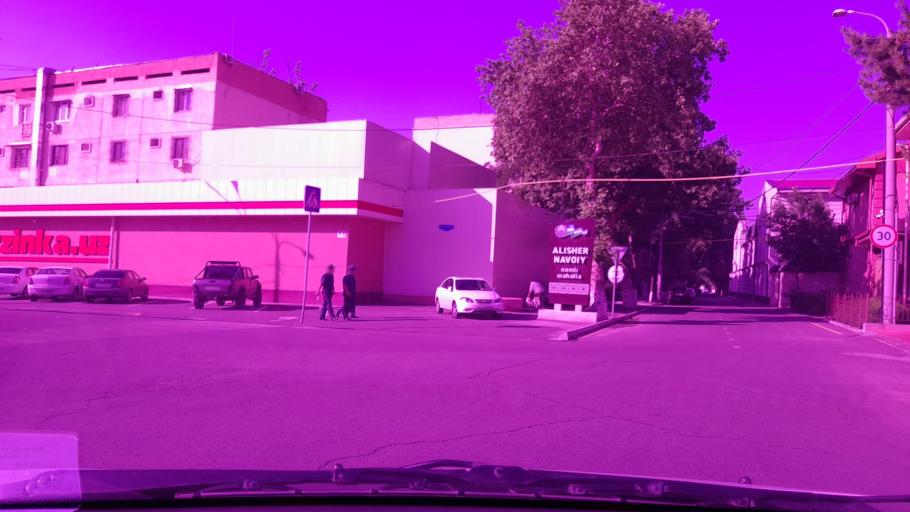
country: UZ
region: Toshkent
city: Salor
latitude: 41.3329
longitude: 69.3627
